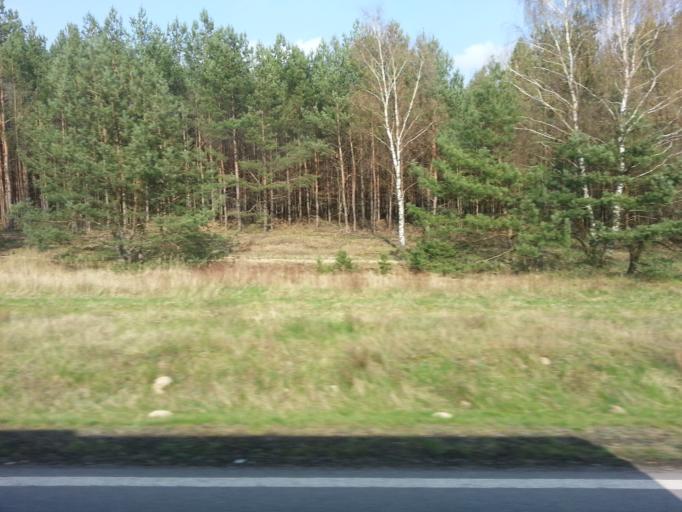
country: DE
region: Brandenburg
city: Walsleben
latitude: 53.0108
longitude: 12.5871
